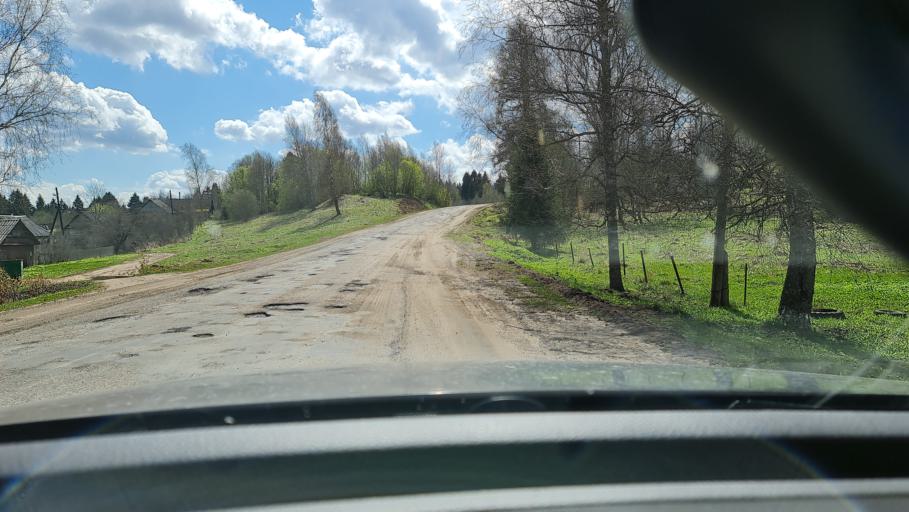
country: RU
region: Tverskaya
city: Toropets
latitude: 56.6428
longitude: 31.4210
